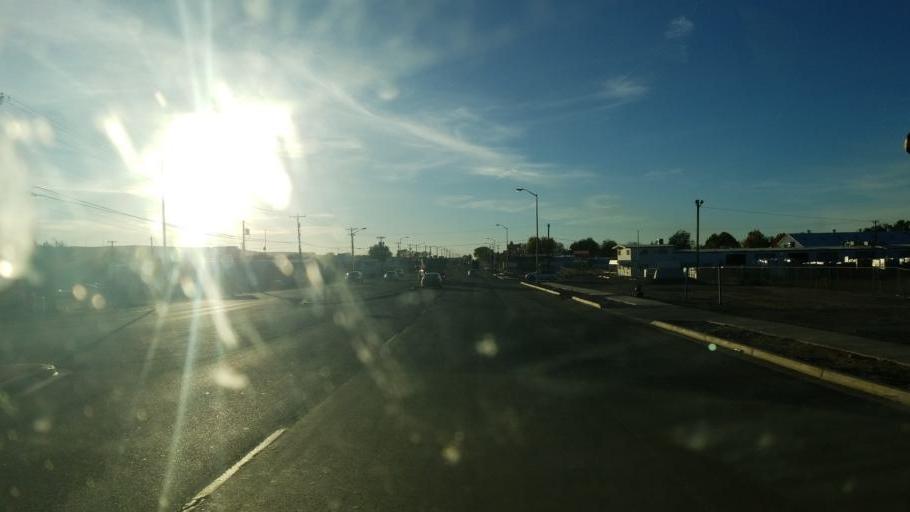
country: US
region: New Mexico
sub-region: San Juan County
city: Farmington
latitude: 36.7194
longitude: -108.1681
